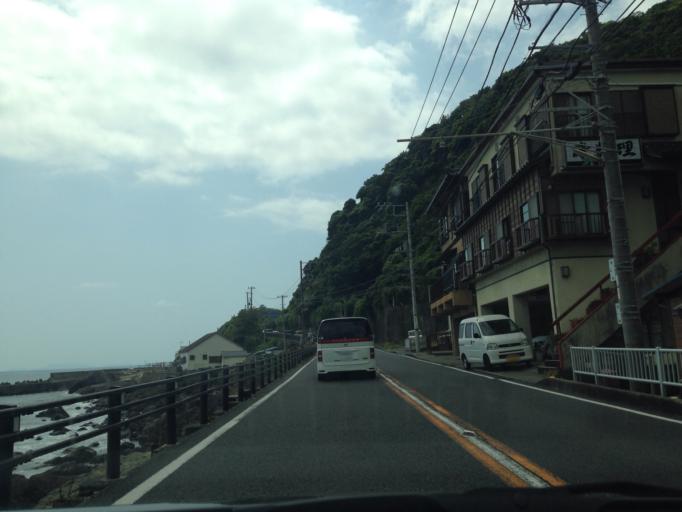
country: JP
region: Shizuoka
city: Shimoda
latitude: 34.7407
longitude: 138.9986
